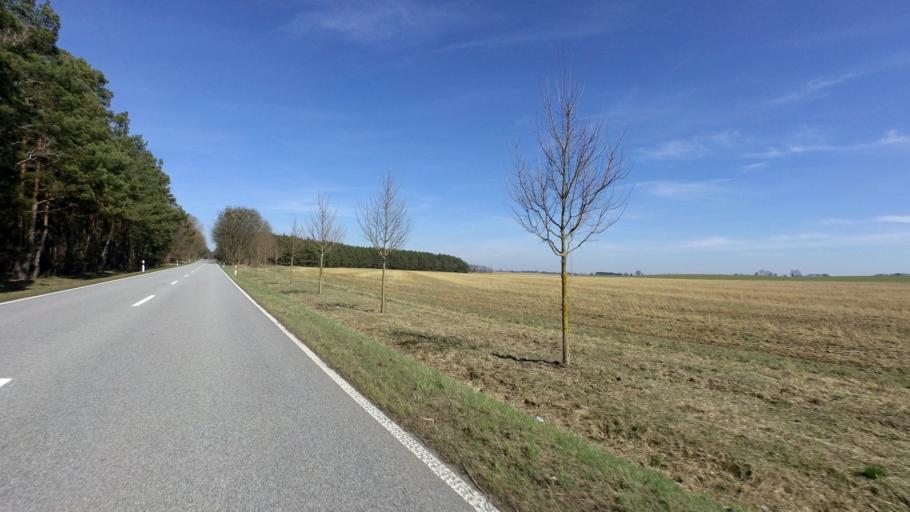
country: DE
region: Brandenburg
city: Waldsieversdorf
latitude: 52.4724
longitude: 14.0618
